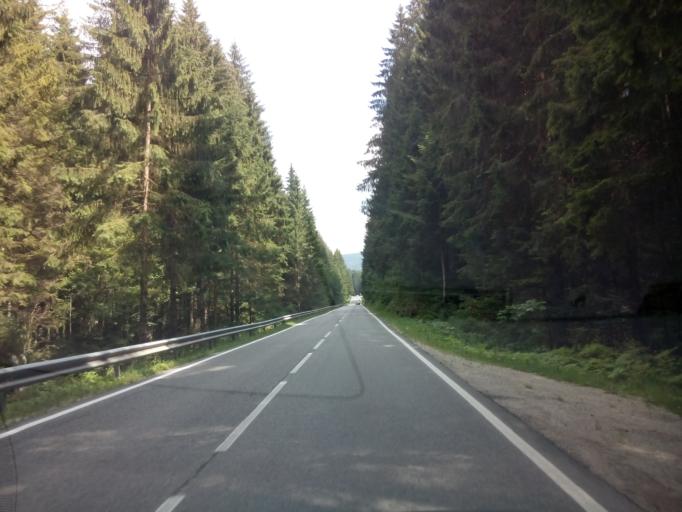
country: IT
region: Veneto
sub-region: Provincia di Vicenza
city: Asiago
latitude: 45.8550
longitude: 11.5287
